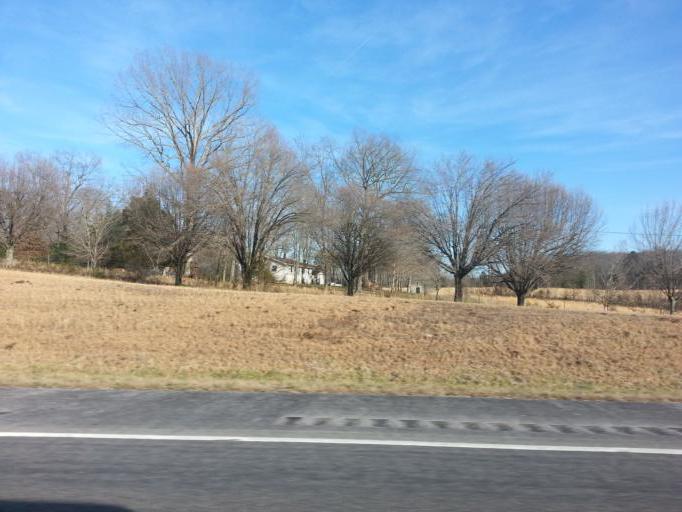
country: US
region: Tennessee
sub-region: Warren County
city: McMinnville
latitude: 35.7601
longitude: -85.6293
